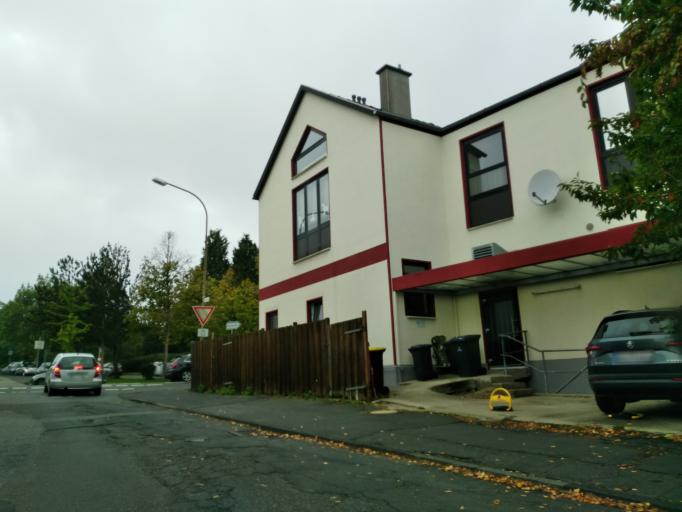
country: DE
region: Rheinland-Pfalz
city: Windhagen
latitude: 50.6620
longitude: 7.3027
